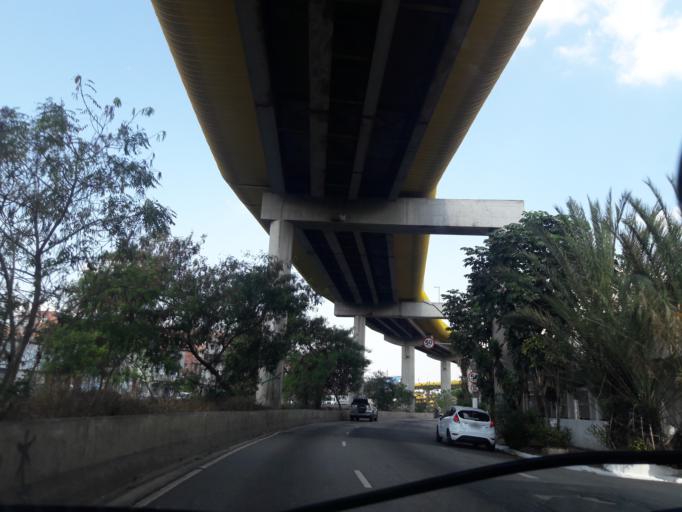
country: BR
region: Sao Paulo
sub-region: Sao Paulo
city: Sao Paulo
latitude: -23.5711
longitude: -46.6045
